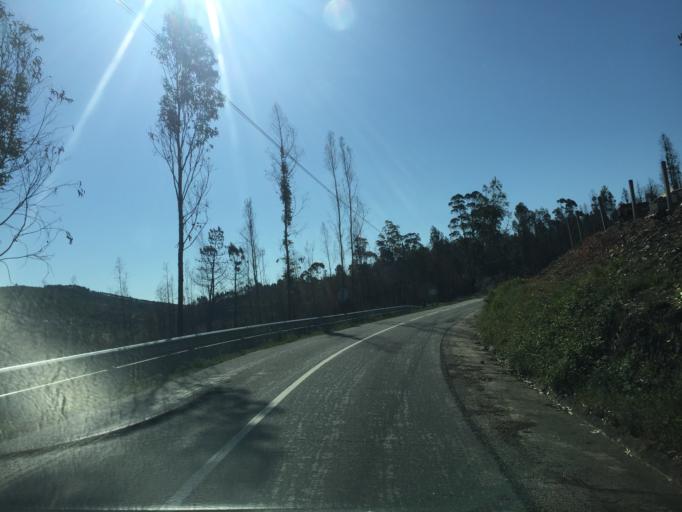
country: PT
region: Coimbra
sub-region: Pampilhosa da Serra
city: Pampilhosa da Serra
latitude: 40.0433
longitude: -7.8983
